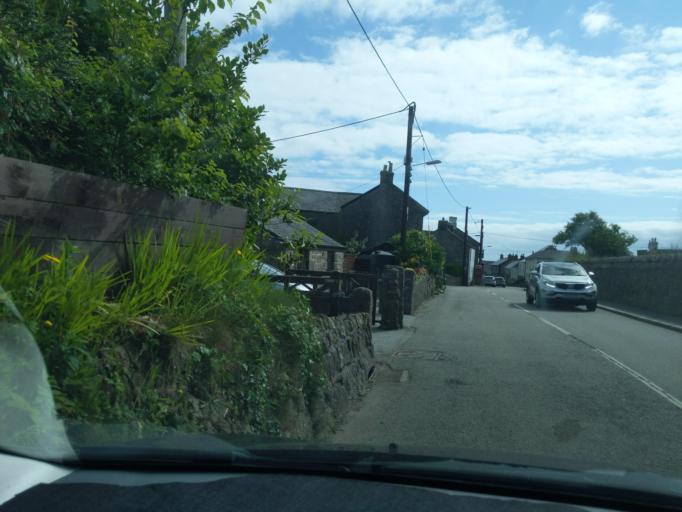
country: GB
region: England
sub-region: Cornwall
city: St. Buryan
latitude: 50.0750
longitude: -5.6219
